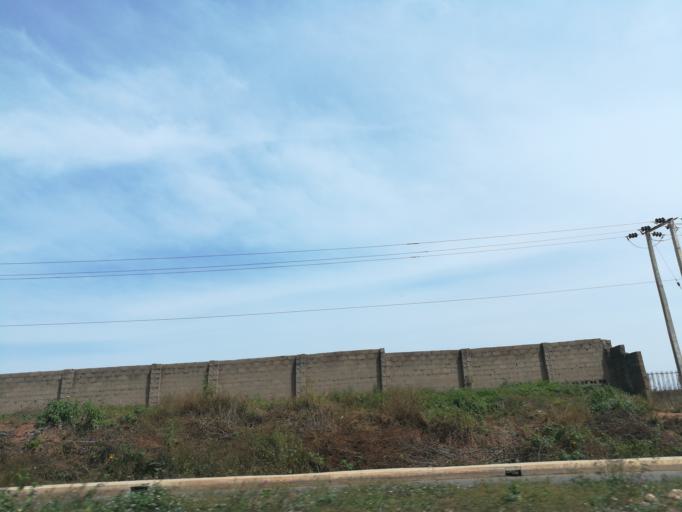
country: NG
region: Plateau
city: Bukuru
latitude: 9.8212
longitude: 8.8652
